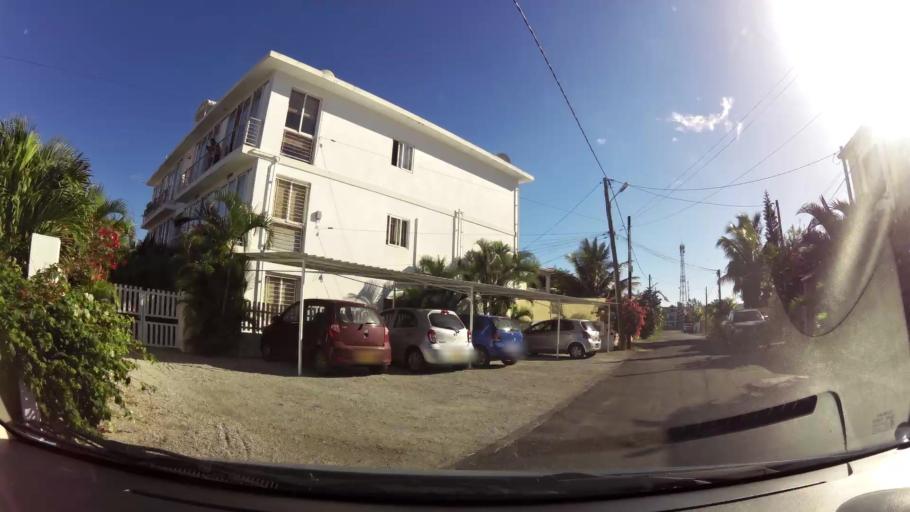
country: MU
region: Black River
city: Grande Riviere Noire
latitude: -20.3539
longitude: 57.3632
